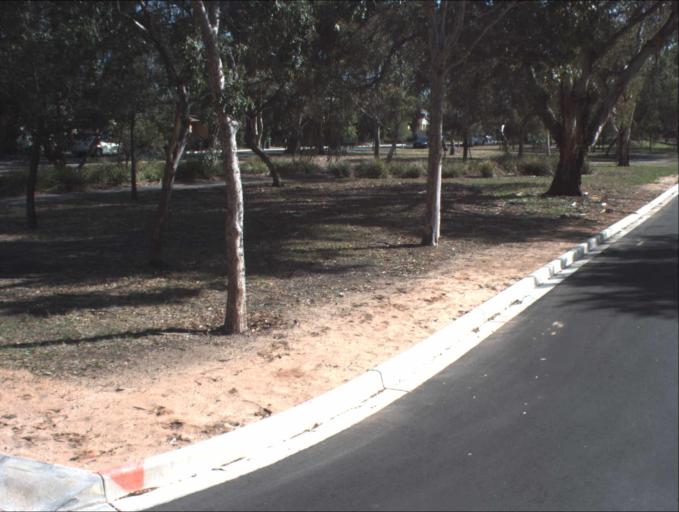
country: AU
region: South Australia
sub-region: Port Adelaide Enfield
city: Gilles Plains
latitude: -34.8623
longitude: 138.6403
